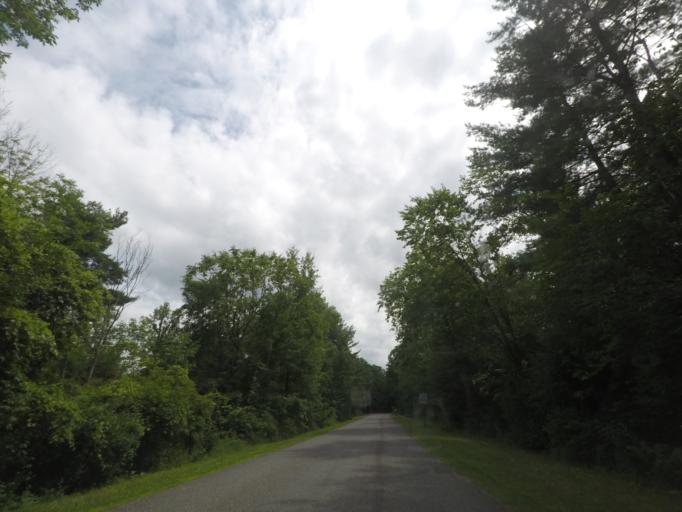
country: US
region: New York
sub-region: Saratoga County
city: Stillwater
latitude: 43.0143
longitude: -73.6458
